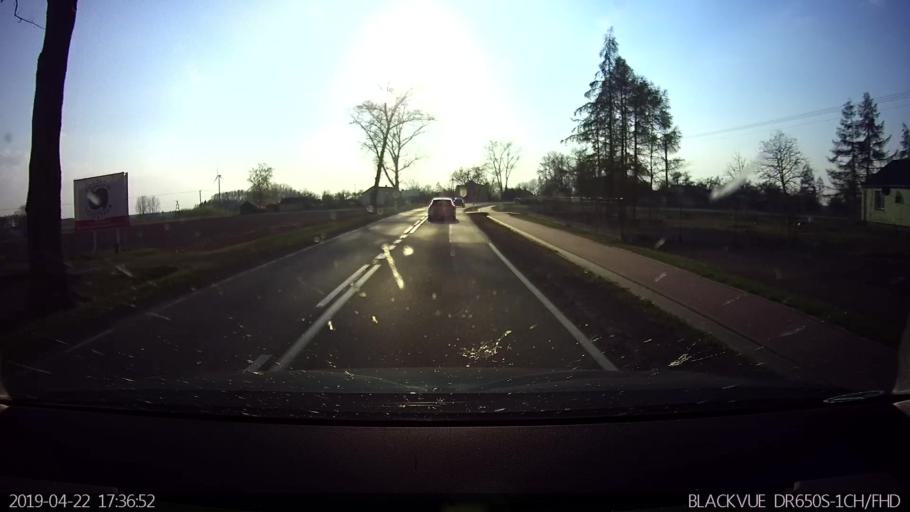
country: PL
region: Masovian Voivodeship
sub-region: Powiat sokolowski
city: Sokolow Podlaski
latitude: 52.4075
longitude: 22.1828
